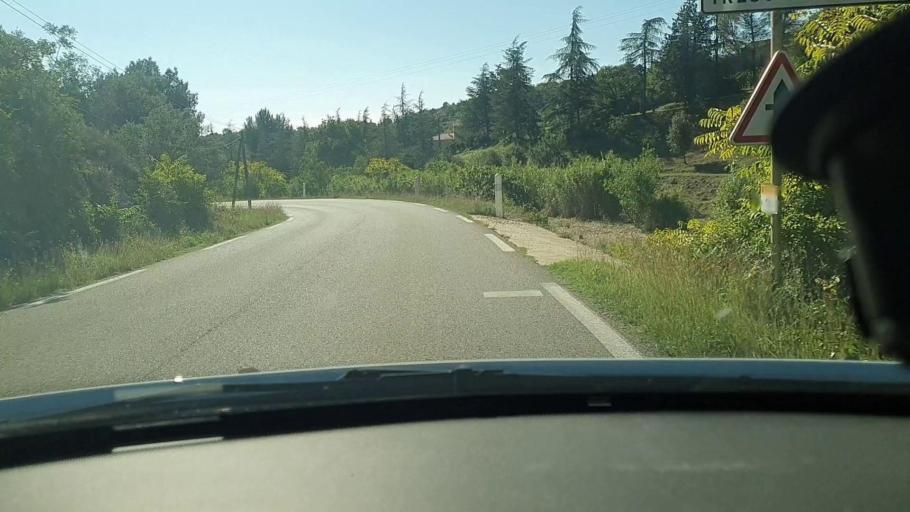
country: FR
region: Languedoc-Roussillon
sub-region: Departement du Gard
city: Saint-Julien-de-Peyrolas
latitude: 44.2971
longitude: 4.5228
